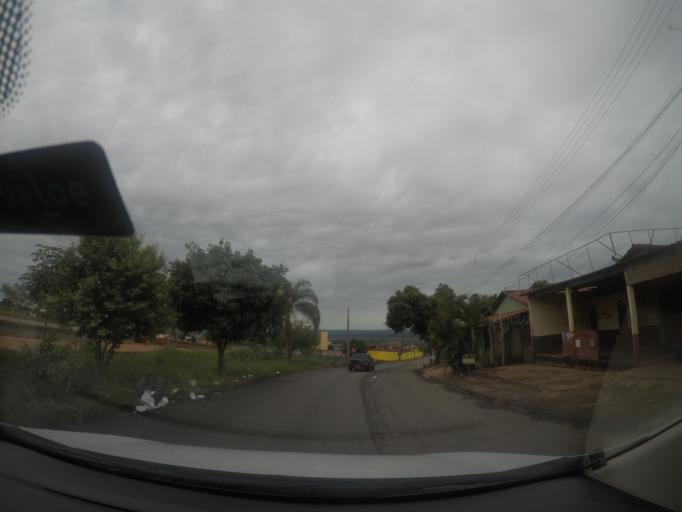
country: BR
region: Goias
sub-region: Goiania
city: Goiania
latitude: -16.6110
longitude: -49.3125
